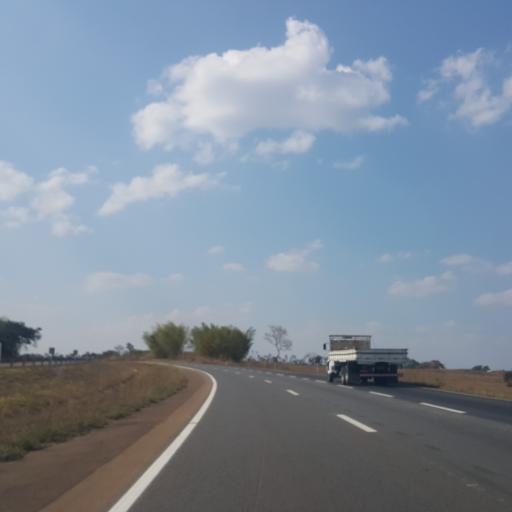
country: BR
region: Goias
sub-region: Abadiania
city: Abadiania
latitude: -16.2943
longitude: -48.8007
